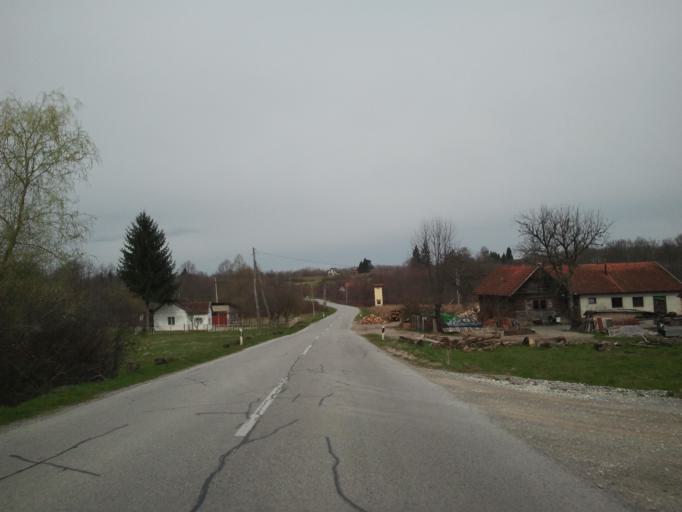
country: HR
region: Sisacko-Moslavacka
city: Gvozd
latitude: 45.3168
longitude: 15.9621
